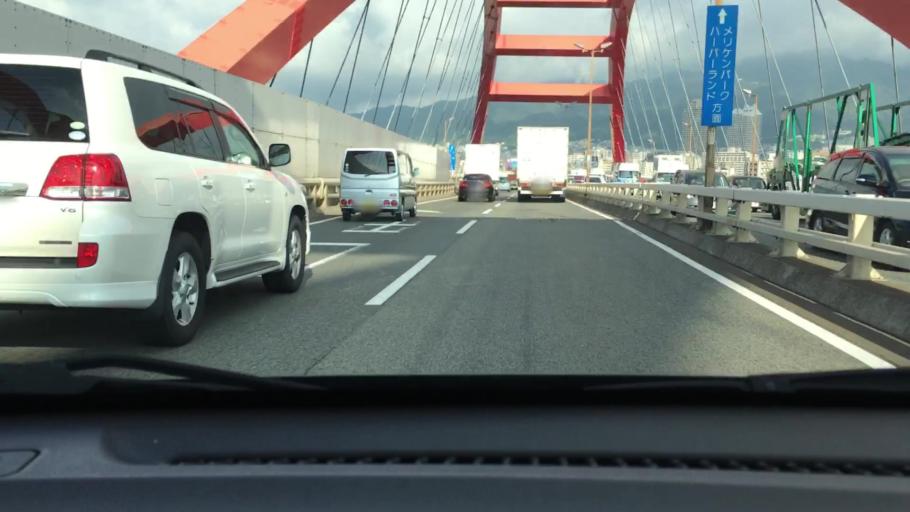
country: JP
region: Hyogo
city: Ashiya
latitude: 34.7073
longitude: 135.2518
